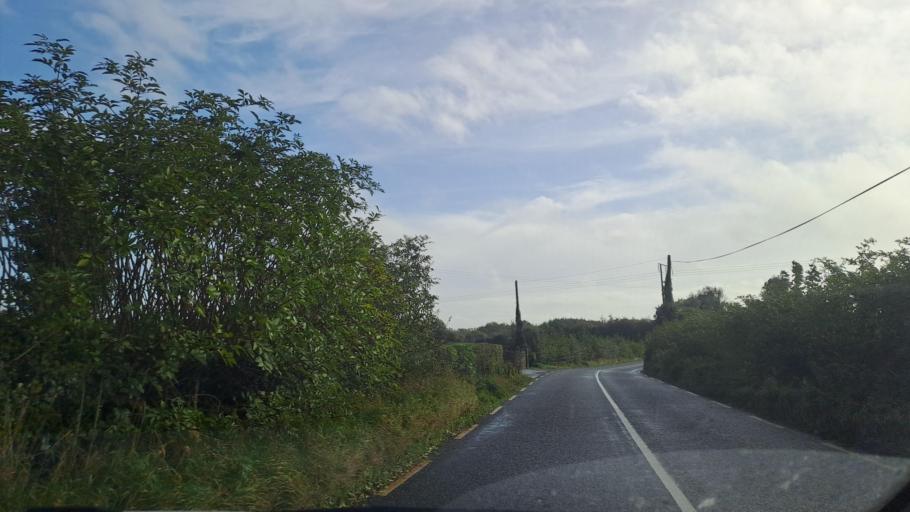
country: IE
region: Ulster
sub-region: County Monaghan
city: Carrickmacross
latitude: 53.9172
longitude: -6.7096
